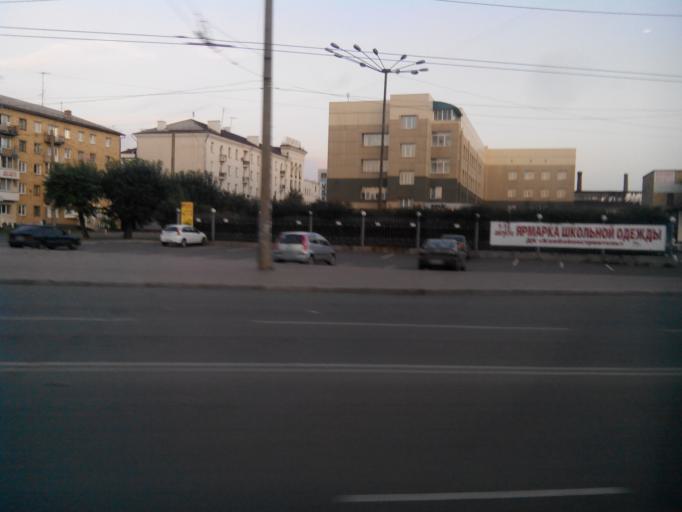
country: RU
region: Krasnoyarskiy
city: Krasnoyarsk
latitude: 56.0075
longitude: 92.8369
